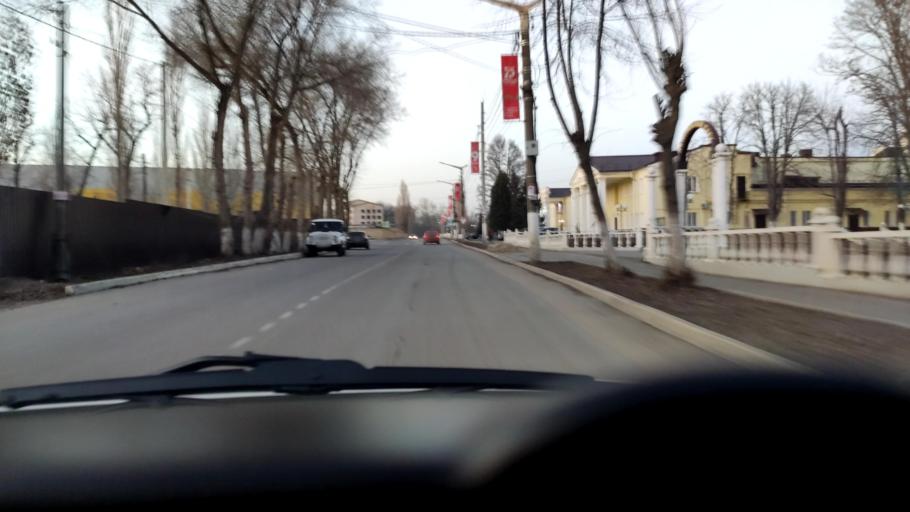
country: RU
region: Voronezj
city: Semiluki
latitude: 51.6863
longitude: 39.0397
